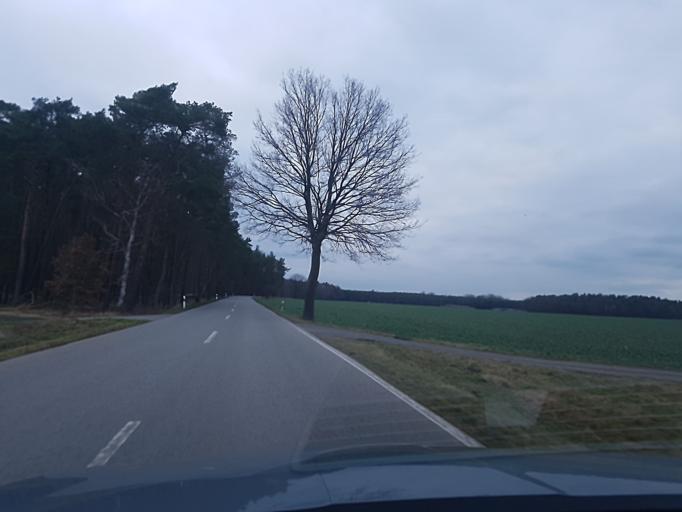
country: DE
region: Brandenburg
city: Finsterwalde
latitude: 51.6707
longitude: 13.6924
